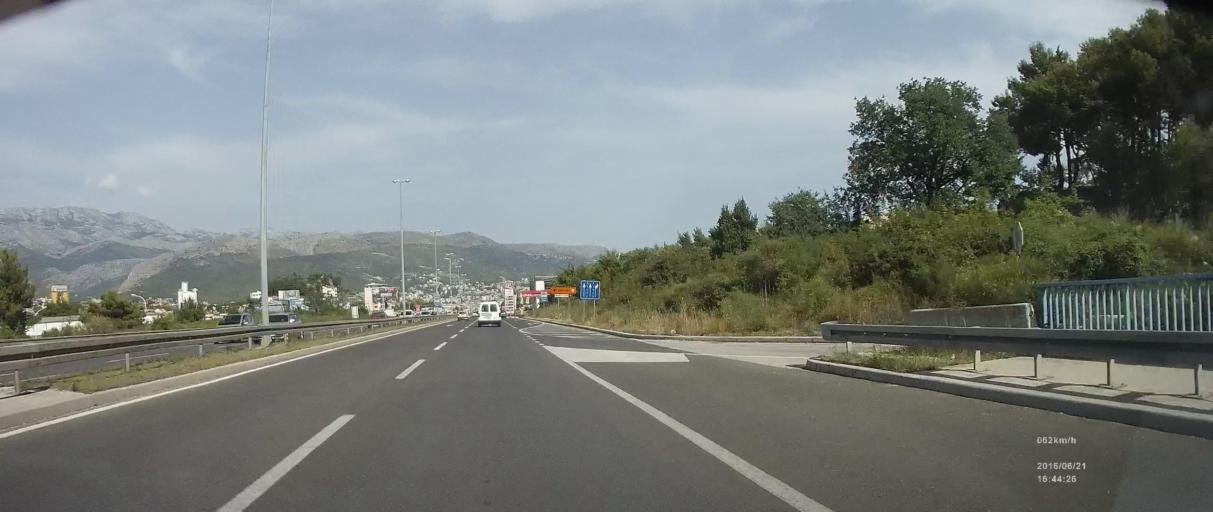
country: HR
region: Splitsko-Dalmatinska
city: Kamen
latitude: 43.5086
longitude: 16.4967
